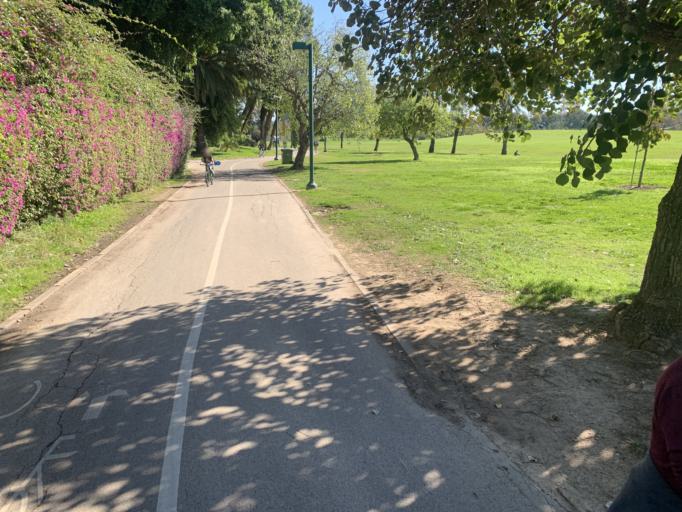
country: IL
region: Tel Aviv
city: Ramat Gan
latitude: 32.1009
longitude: 34.8100
